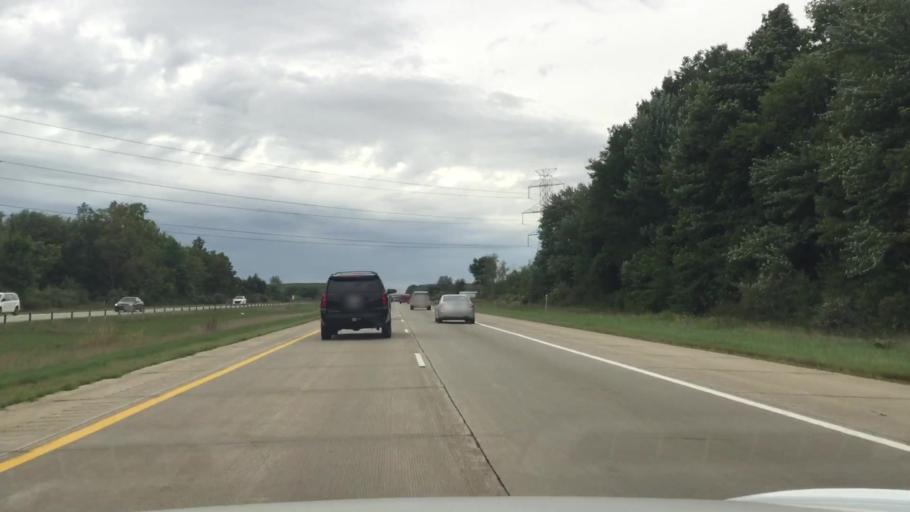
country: US
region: Michigan
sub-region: Macomb County
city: Richmond
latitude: 42.7723
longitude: -82.6832
